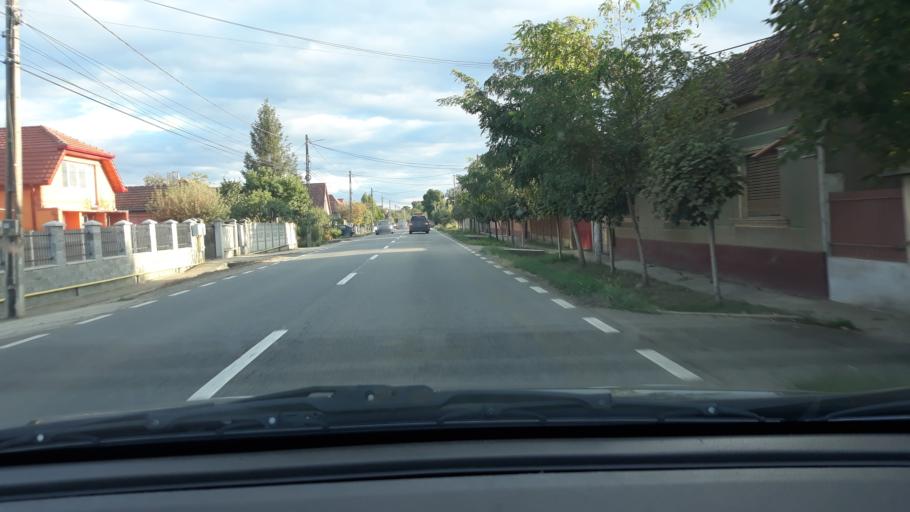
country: RO
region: Bihor
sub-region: Comuna Biharea
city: Biharea
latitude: 47.1644
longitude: 21.9221
